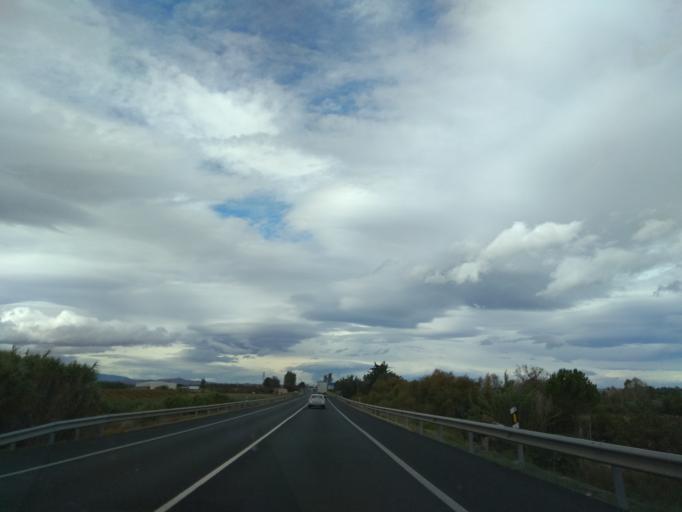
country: ES
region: La Rioja
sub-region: Provincia de La Rioja
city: Alfaro
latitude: 42.1691
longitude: -1.7569
